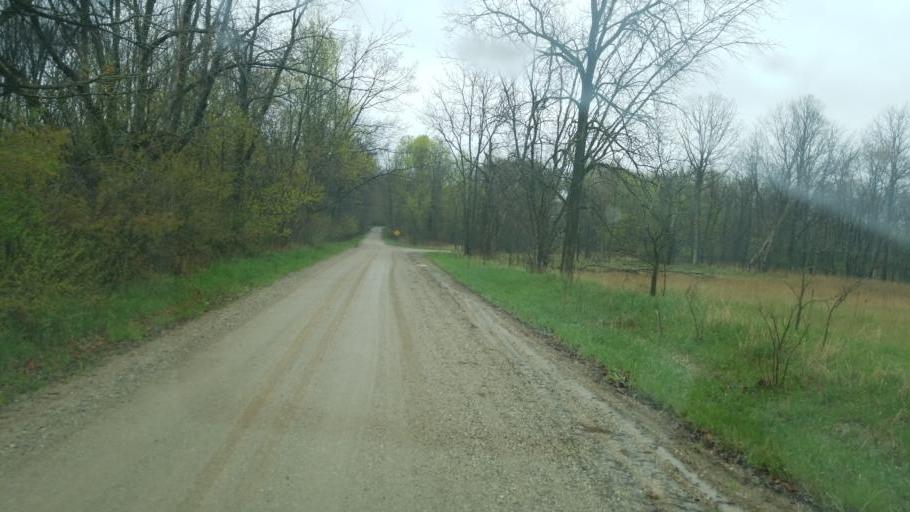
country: US
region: Michigan
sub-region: Mecosta County
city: Canadian Lakes
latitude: 43.5037
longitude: -85.3330
